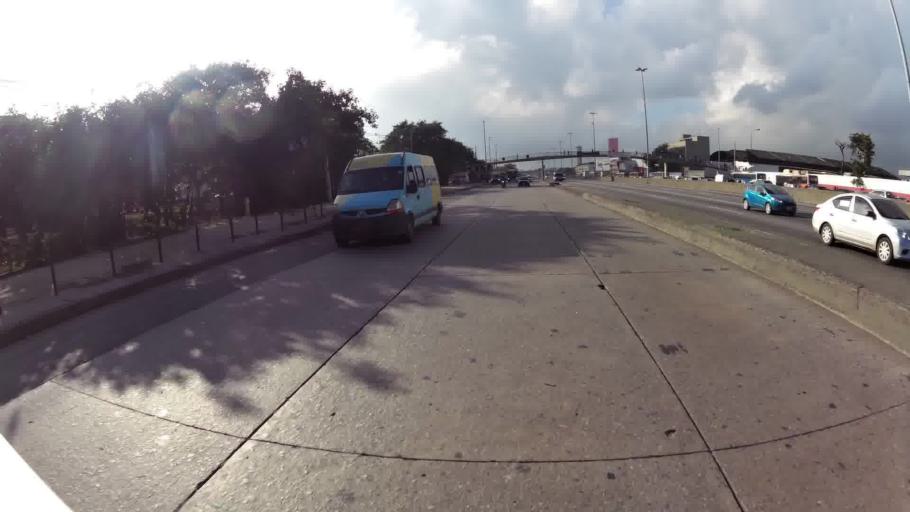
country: BR
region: Rio de Janeiro
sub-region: Duque De Caxias
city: Duque de Caxias
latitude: -22.8188
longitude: -43.2849
